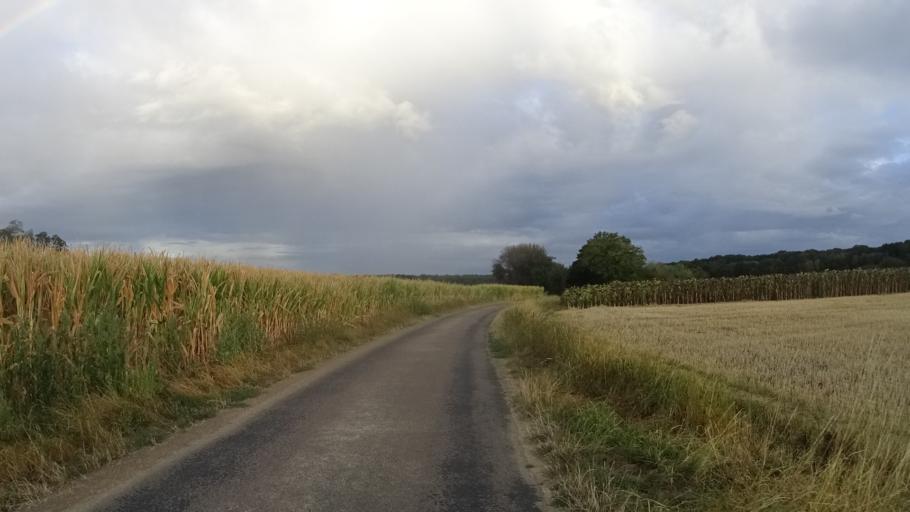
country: FR
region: Bourgogne
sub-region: Departement de Saone-et-Loire
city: Verdun-sur-le-Doubs
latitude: 46.9536
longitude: 5.0590
